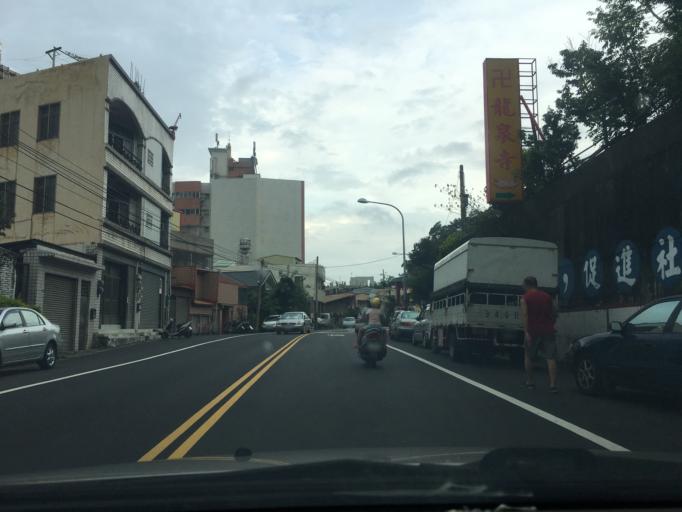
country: TW
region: Taiwan
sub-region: Changhua
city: Chang-hua
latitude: 24.0735
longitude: 120.5576
